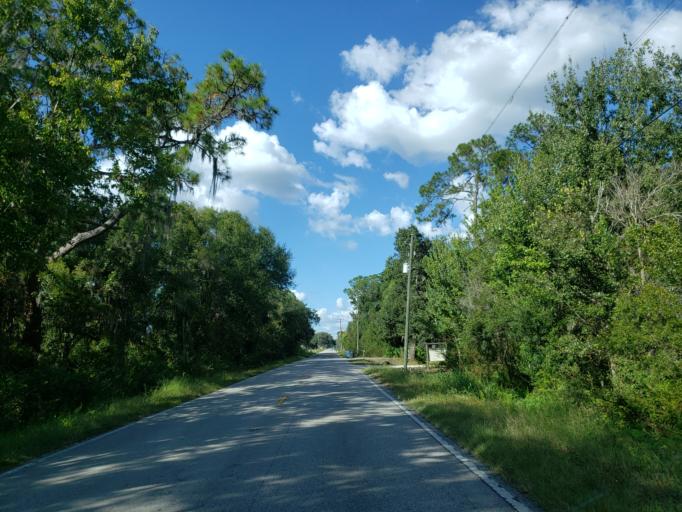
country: US
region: Florida
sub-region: Hillsborough County
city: Dover
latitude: 27.9835
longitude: -82.1869
